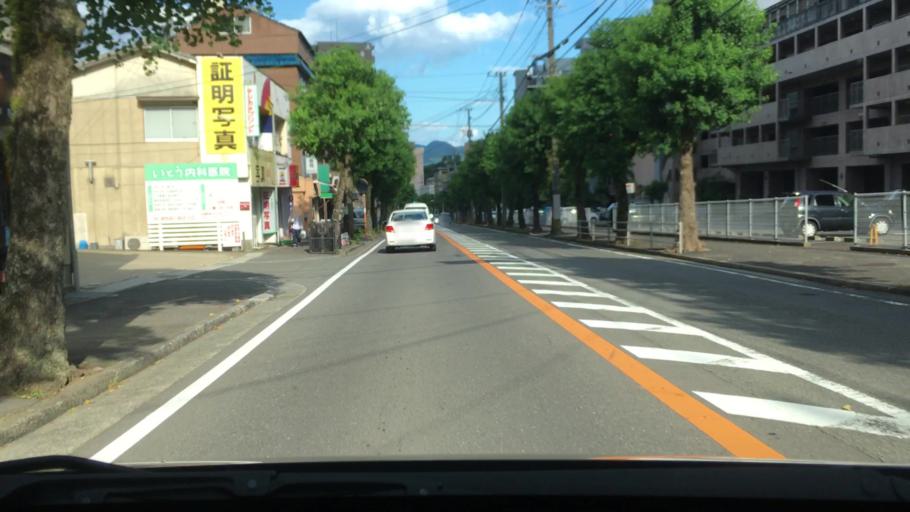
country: JP
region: Nagasaki
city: Togitsu
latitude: 32.8084
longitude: 129.8329
